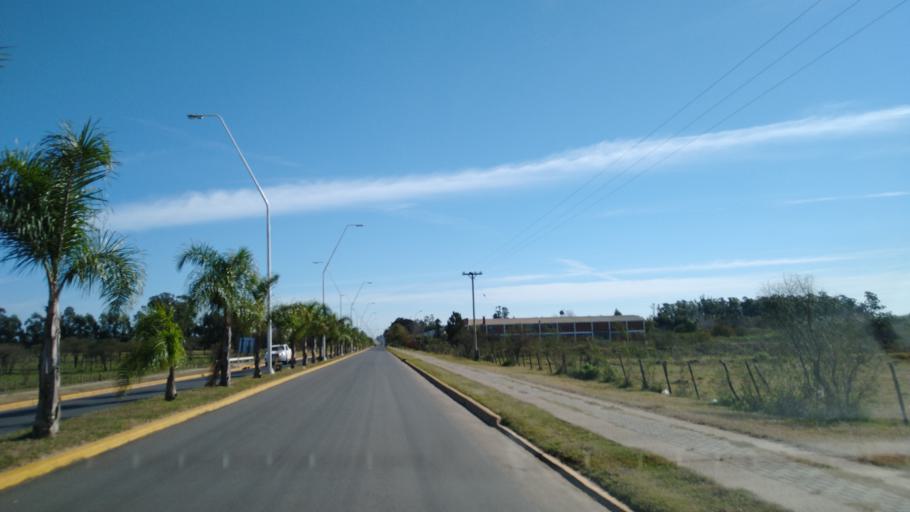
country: AR
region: Entre Rios
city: Chajari
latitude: -30.7504
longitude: -58.0088
